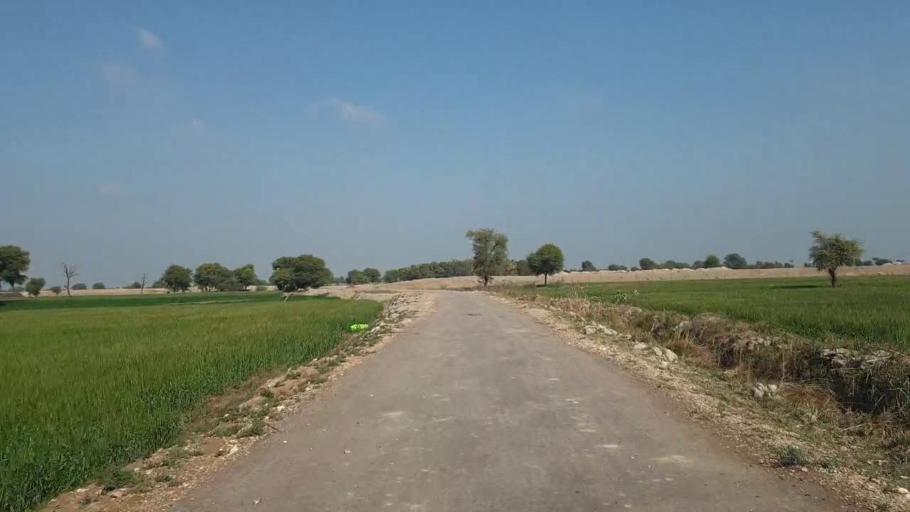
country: PK
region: Sindh
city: Shahdadpur
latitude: 26.0275
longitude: 68.6154
